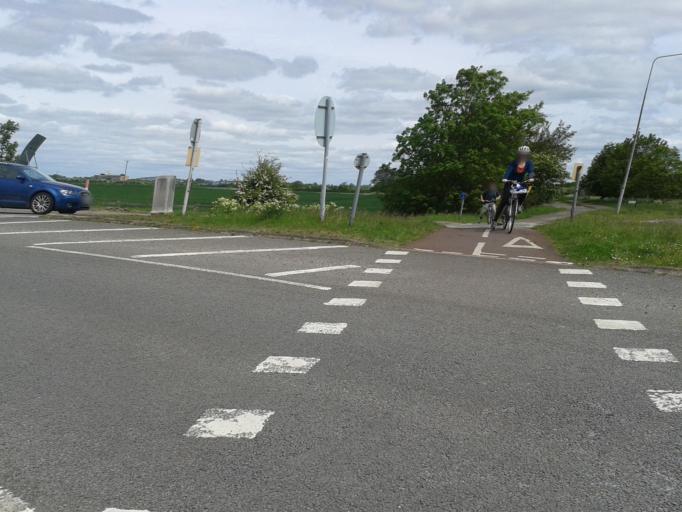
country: GB
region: England
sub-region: Cambridgeshire
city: Grantchester
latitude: 52.1915
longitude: 0.0773
